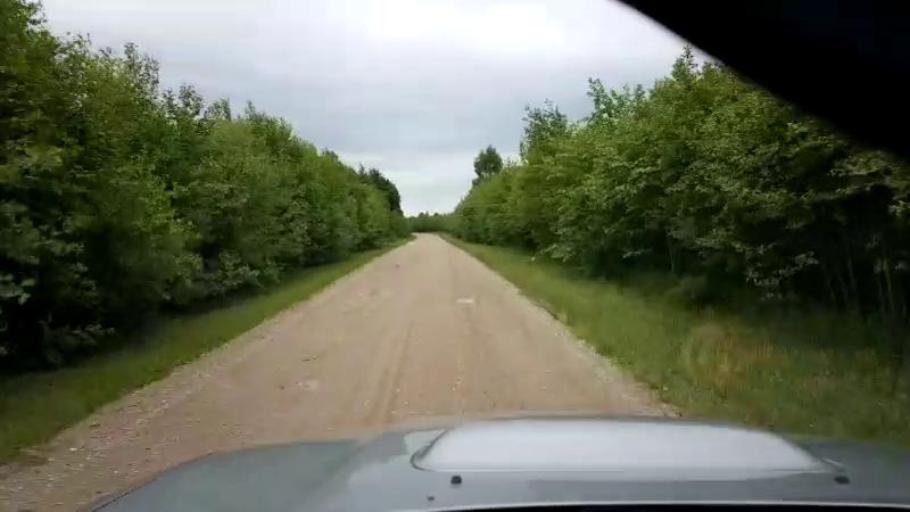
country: EE
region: Paernumaa
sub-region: Halinga vald
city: Parnu-Jaagupi
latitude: 58.5557
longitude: 24.5618
